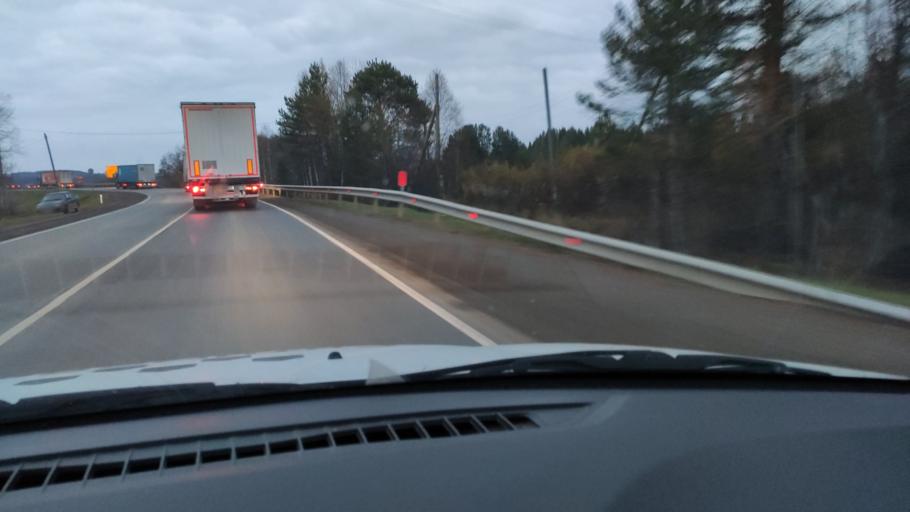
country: RU
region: Kirov
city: Kostino
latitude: 58.8529
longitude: 53.2163
